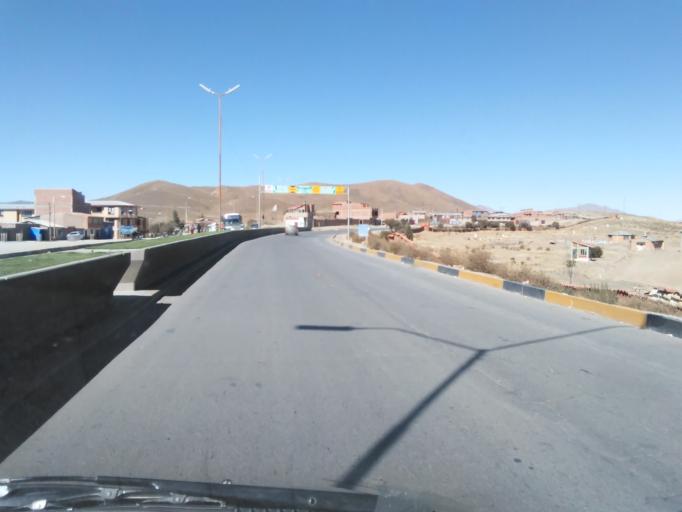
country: BO
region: Oruro
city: Oruro
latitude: -17.9795
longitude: -67.0521
